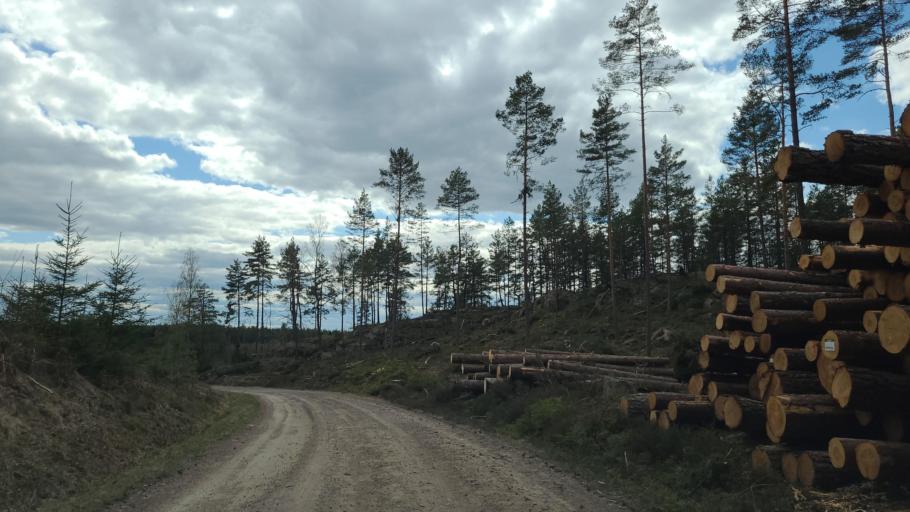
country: SE
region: OEstergoetland
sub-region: Norrkopings Kommun
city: Krokek
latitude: 58.6922
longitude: 16.4216
